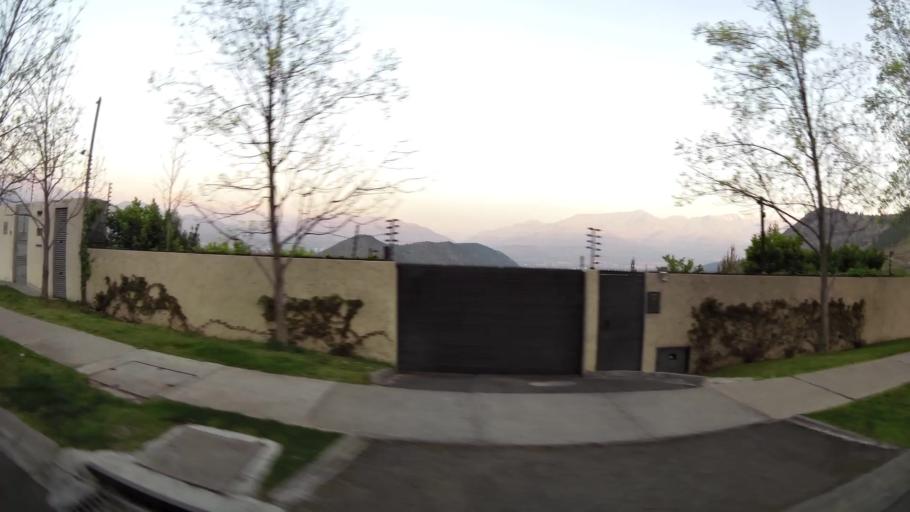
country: CL
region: Santiago Metropolitan
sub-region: Provincia de Chacabuco
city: Chicureo Abajo
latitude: -33.3386
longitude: -70.5594
